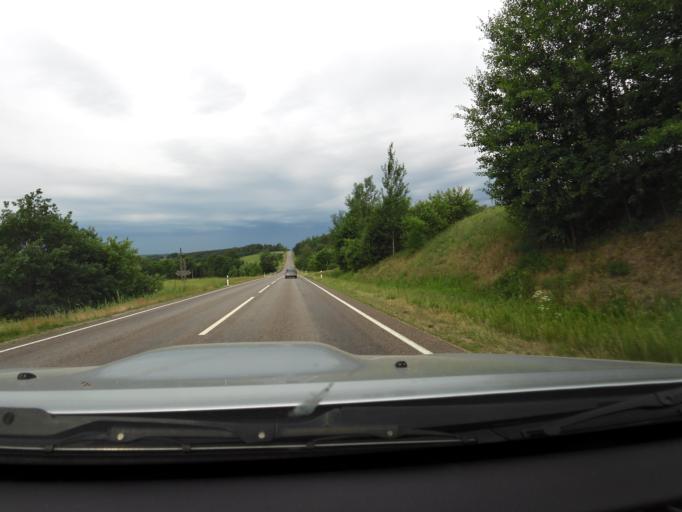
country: LT
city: Aukstadvaris
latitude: 54.5751
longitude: 24.3835
